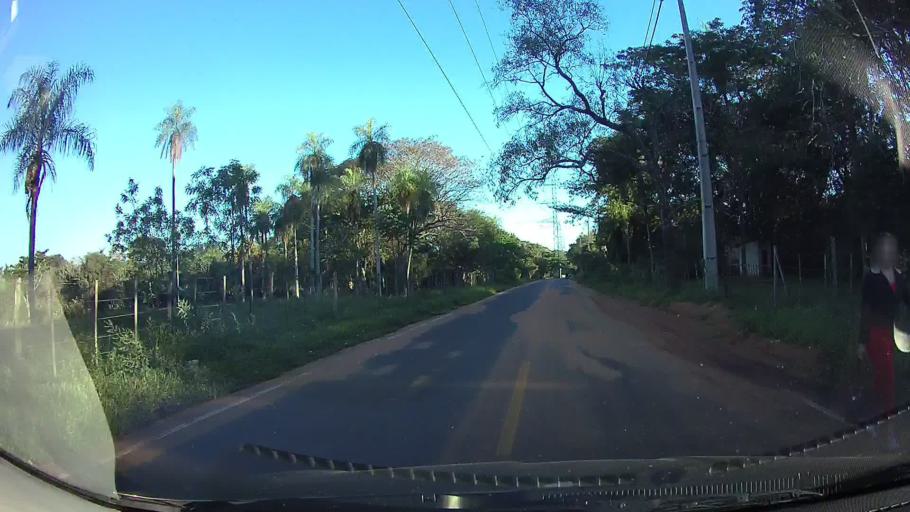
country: PY
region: Central
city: San Lorenzo
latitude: -25.2813
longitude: -57.4657
